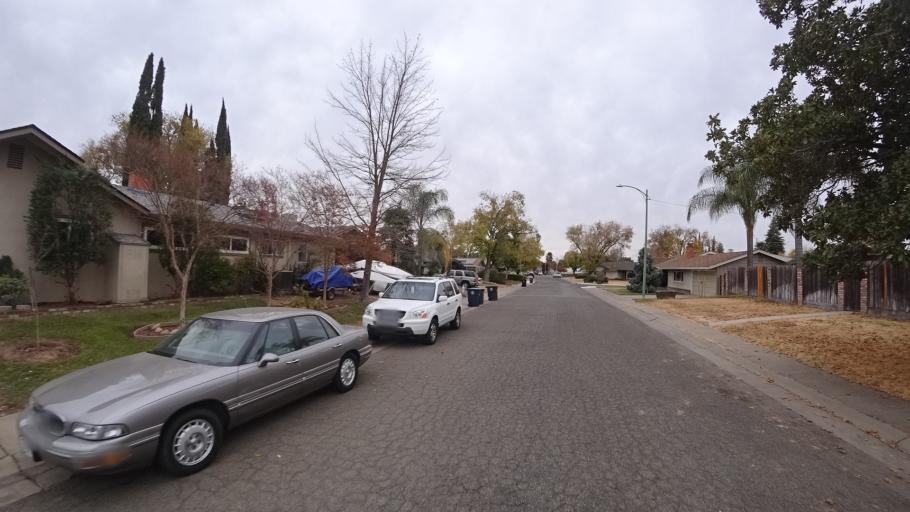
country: US
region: California
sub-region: Sacramento County
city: Citrus Heights
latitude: 38.6959
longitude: -121.2955
